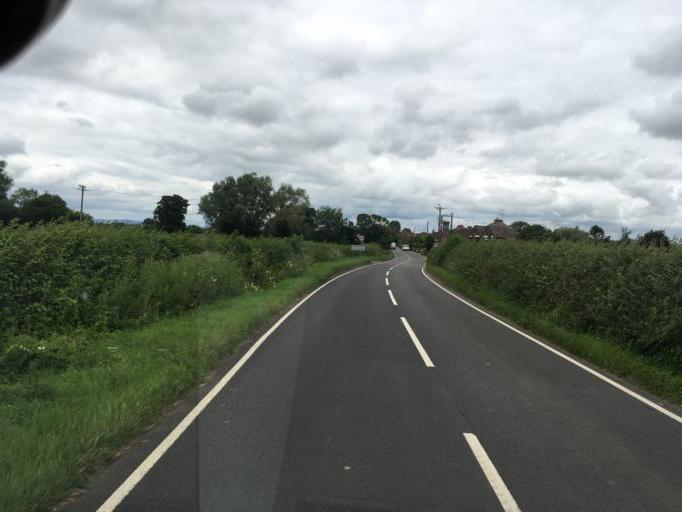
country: GB
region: England
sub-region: Gloucestershire
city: Stonehouse
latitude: 51.7380
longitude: -2.3204
